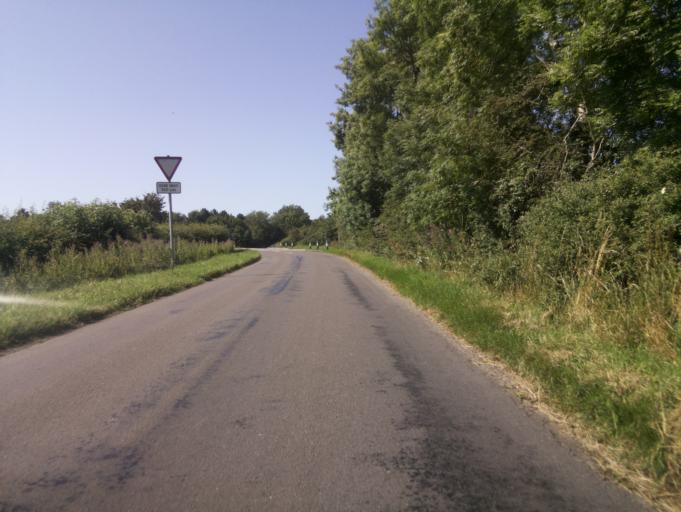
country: GB
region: England
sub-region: Buckinghamshire
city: Buckingham
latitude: 51.9931
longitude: -0.9269
